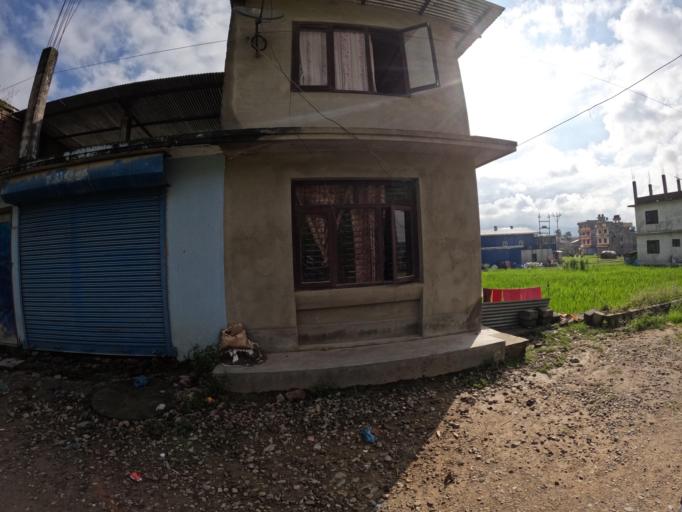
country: NP
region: Central Region
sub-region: Bagmati Zone
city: Kathmandu
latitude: 27.7665
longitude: 85.3328
